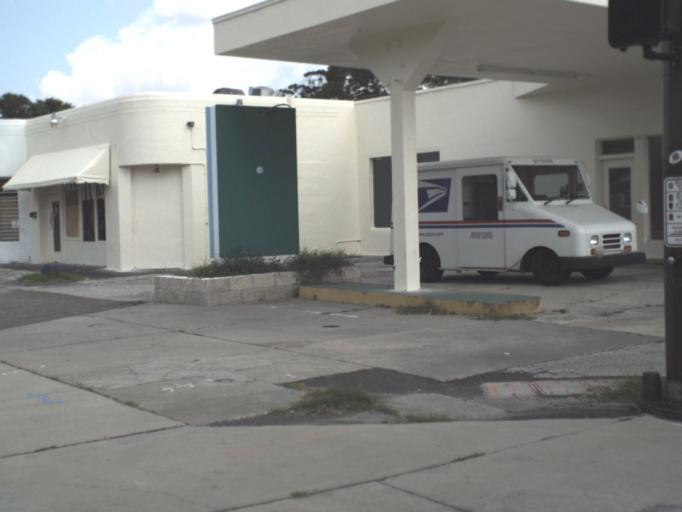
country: US
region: Florida
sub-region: Pinellas County
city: Saint Petersburg
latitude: 27.7774
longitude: -82.6835
